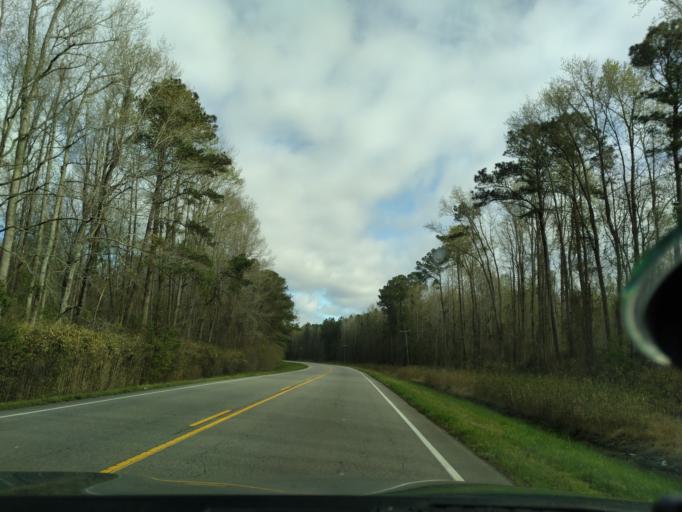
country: US
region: North Carolina
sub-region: Washington County
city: Plymouth
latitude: 35.8808
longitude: -76.6955
